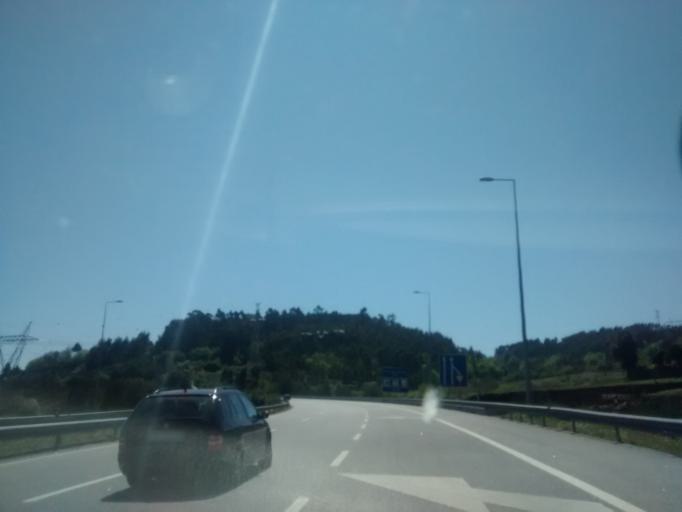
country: PT
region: Braga
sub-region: Guimaraes
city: Candoso
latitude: 41.4242
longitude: -8.3307
